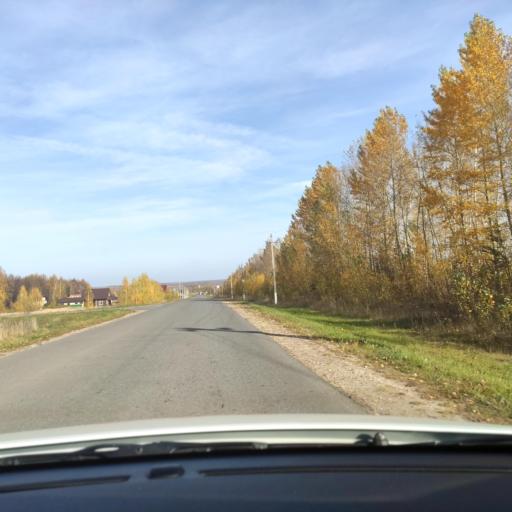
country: RU
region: Tatarstan
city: Pestretsy
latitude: 55.7265
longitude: 49.4584
